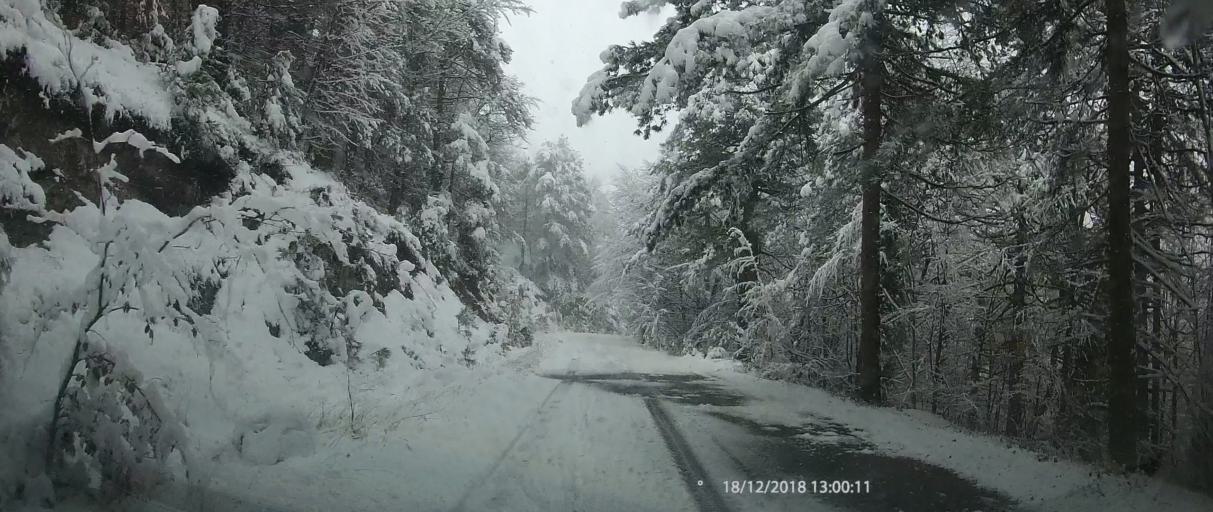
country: GR
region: Central Macedonia
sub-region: Nomos Pierias
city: Litochoro
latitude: 40.1093
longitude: 22.4622
